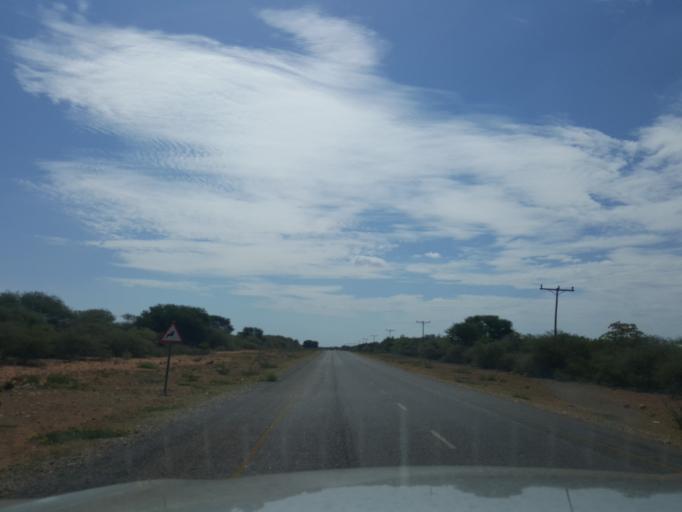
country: BW
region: Kweneng
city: Letlhakeng
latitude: -24.1414
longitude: 25.1454
